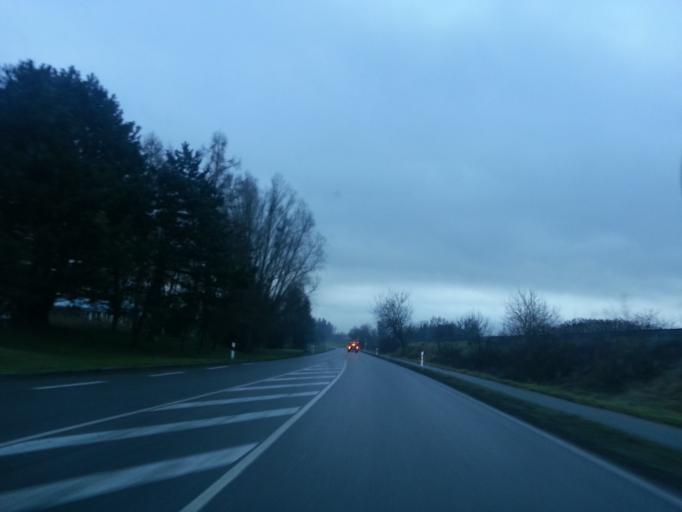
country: DE
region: Baden-Wuerttemberg
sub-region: Tuebingen Region
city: Markdorf
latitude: 47.7078
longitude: 9.3995
